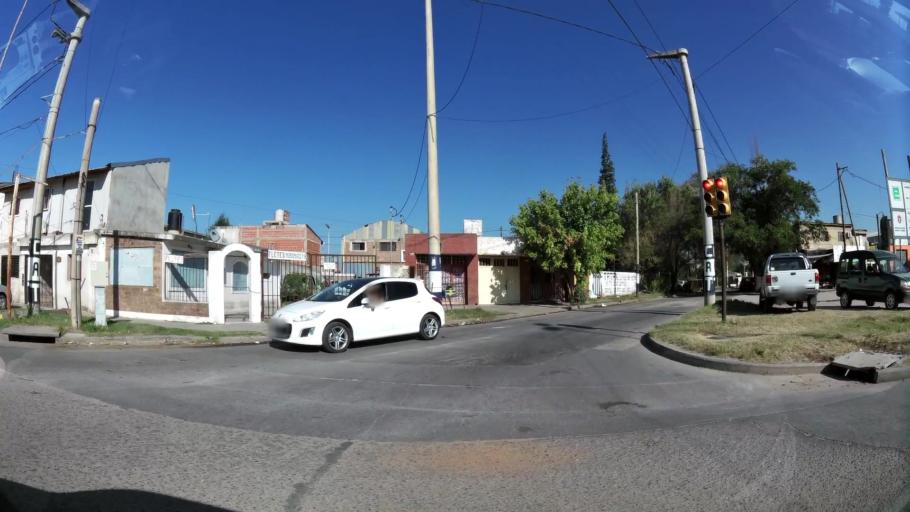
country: AR
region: Cordoba
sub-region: Departamento de Capital
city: Cordoba
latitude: -31.4696
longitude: -64.2273
